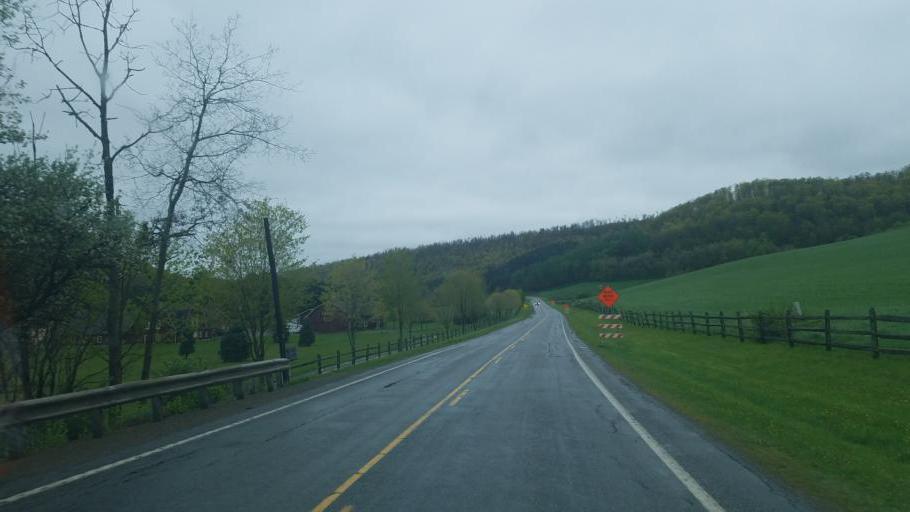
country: US
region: Pennsylvania
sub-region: Potter County
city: Coudersport
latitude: 41.8245
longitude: -77.9648
